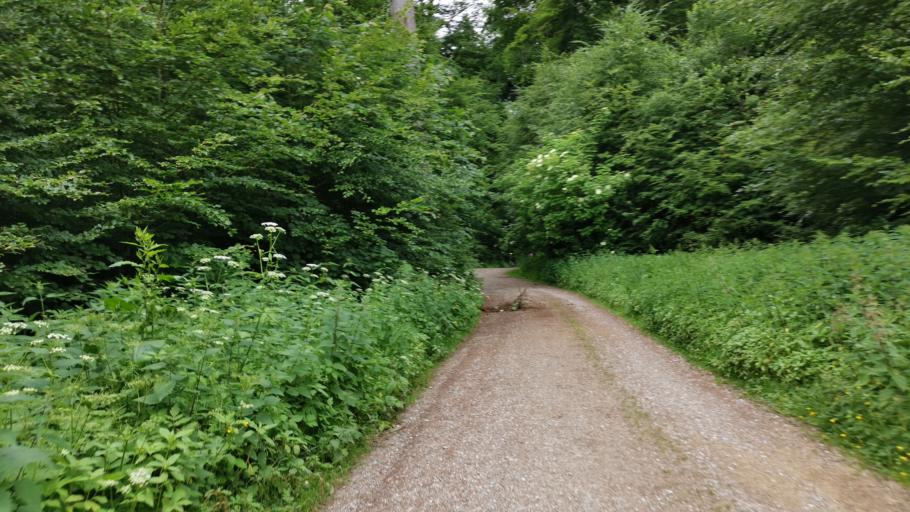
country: DE
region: Bavaria
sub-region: Upper Bavaria
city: Schaftlarn
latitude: 48.0134
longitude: 11.4330
